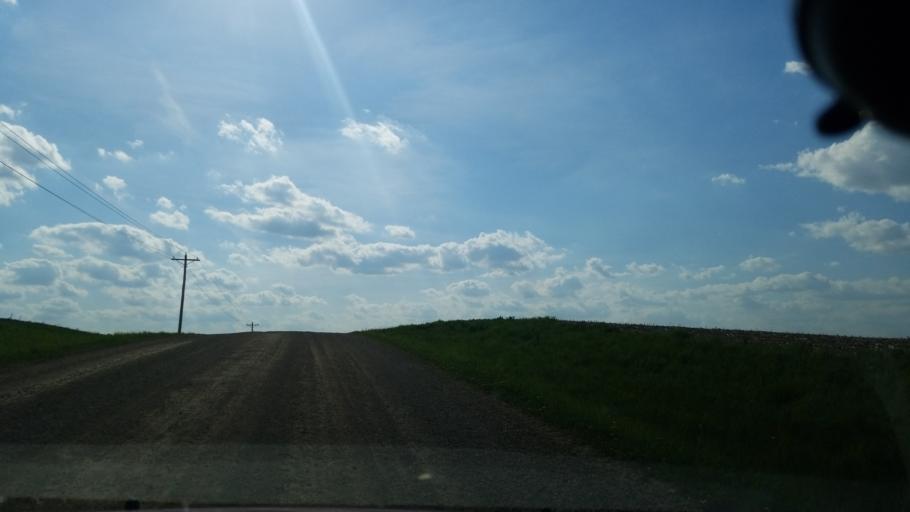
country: US
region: Iowa
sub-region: Jackson County
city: Maquoketa
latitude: 42.2150
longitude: -90.7167
